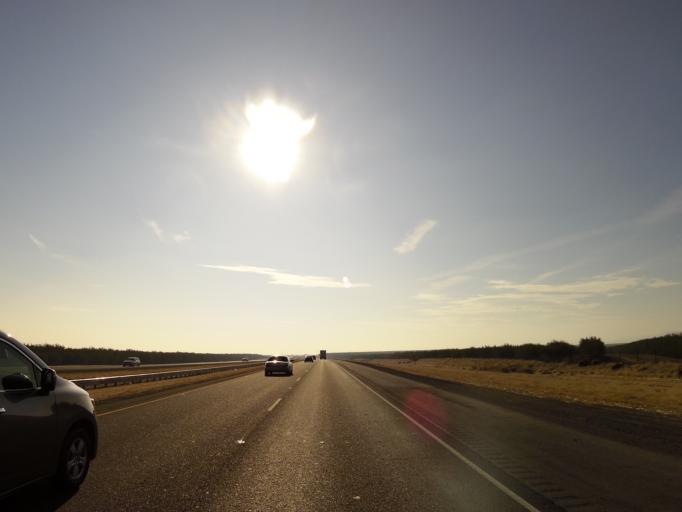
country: US
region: California
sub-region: Merced County
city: South Dos Palos
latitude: 36.7199
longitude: -120.6846
